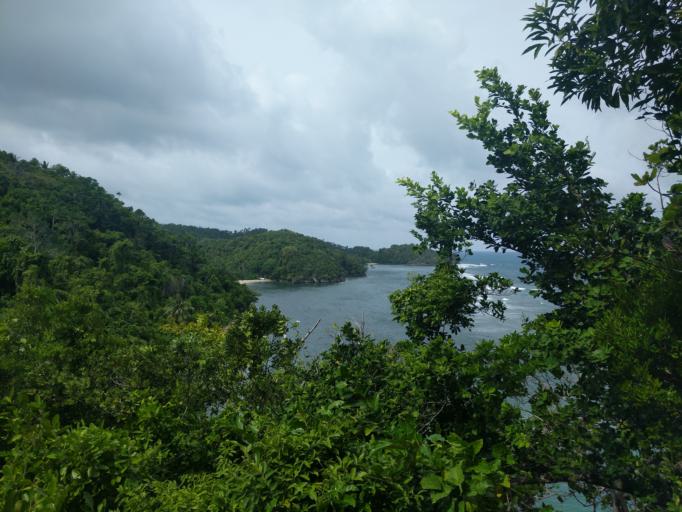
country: PH
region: Western Visayas
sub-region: Province of Negros Occidental
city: Bulata
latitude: 9.8769
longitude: 122.3778
